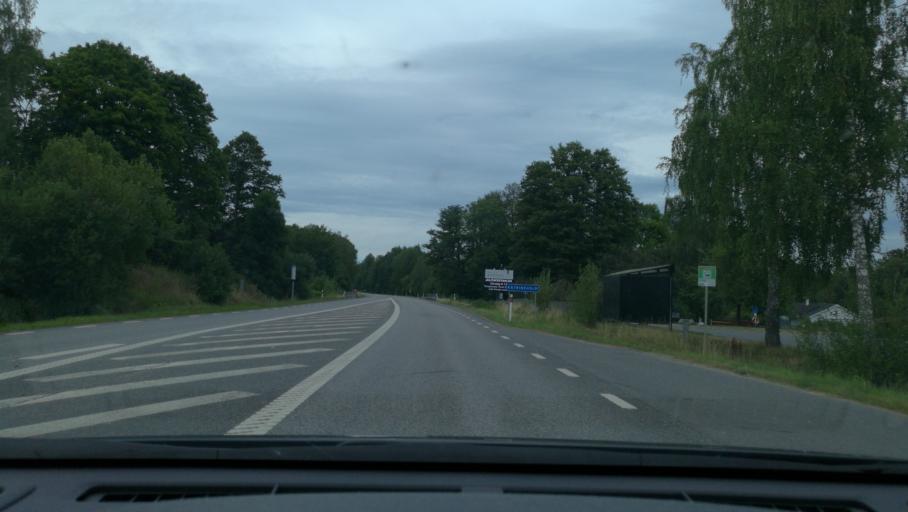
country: SE
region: Soedermanland
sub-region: Katrineholms Kommun
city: Katrineholm
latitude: 58.9669
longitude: 16.1968
